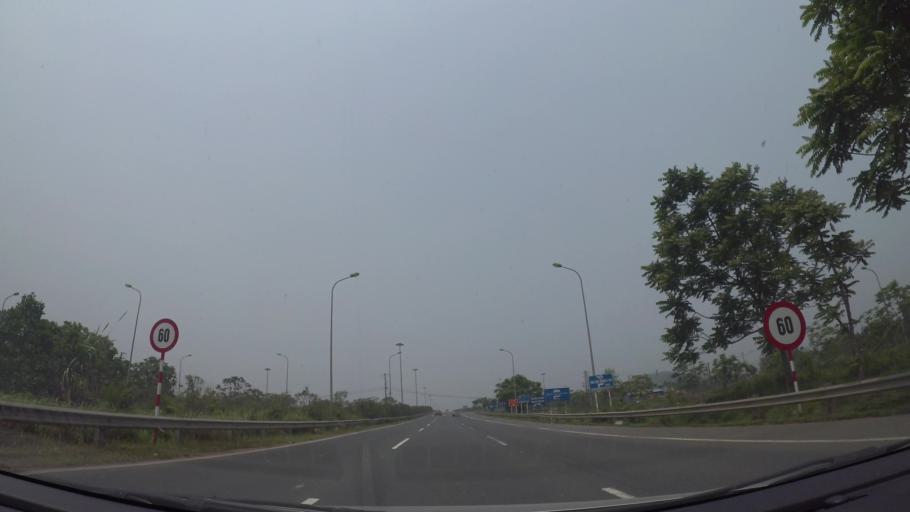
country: VN
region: Ha Noi
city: Lien Quan
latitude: 20.9904
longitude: 105.5302
